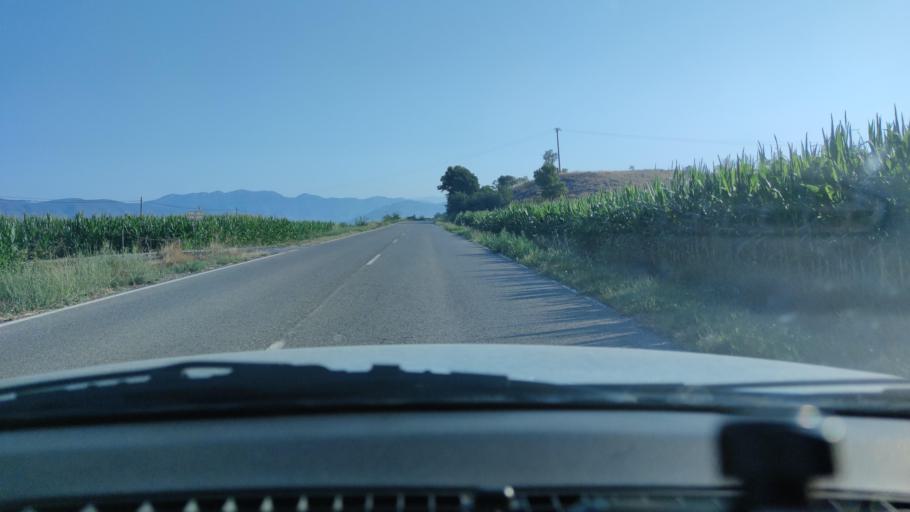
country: ES
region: Catalonia
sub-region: Provincia de Lleida
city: Balaguer
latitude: 41.8039
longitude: 0.8261
